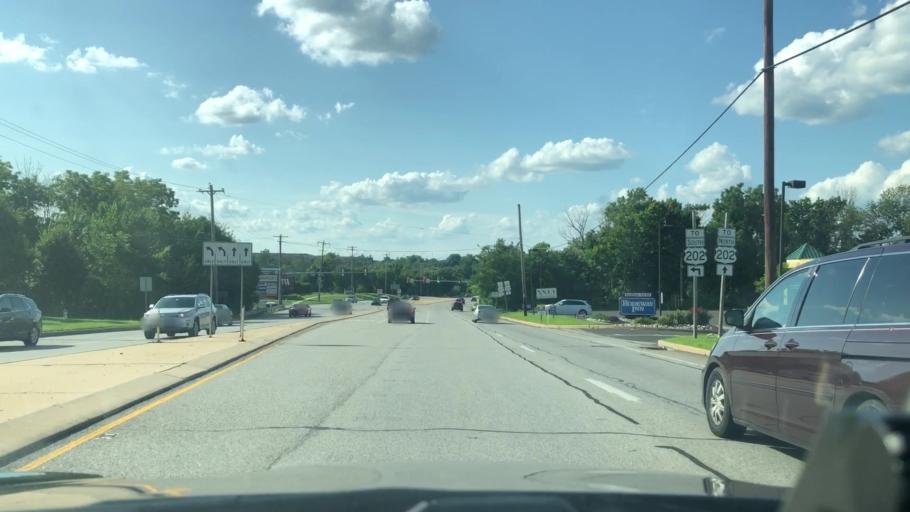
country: US
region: Pennsylvania
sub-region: Montgomery County
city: Montgomeryville
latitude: 40.2277
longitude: -75.2358
